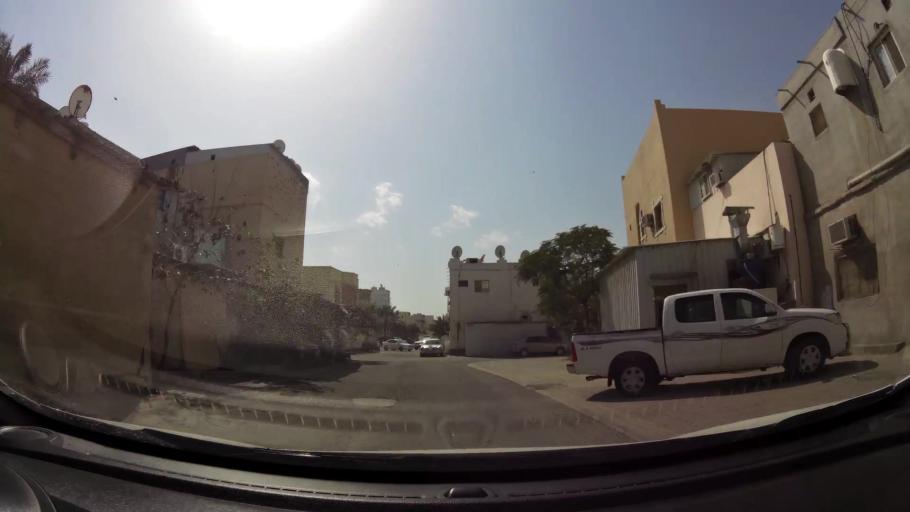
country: BH
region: Manama
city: Jidd Hafs
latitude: 26.2090
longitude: 50.4592
